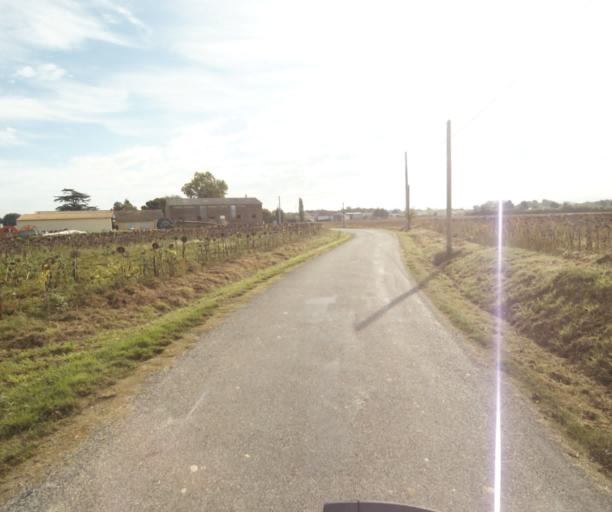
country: FR
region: Midi-Pyrenees
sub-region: Departement du Tarn-et-Garonne
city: Montech
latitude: 43.9482
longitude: 1.2285
